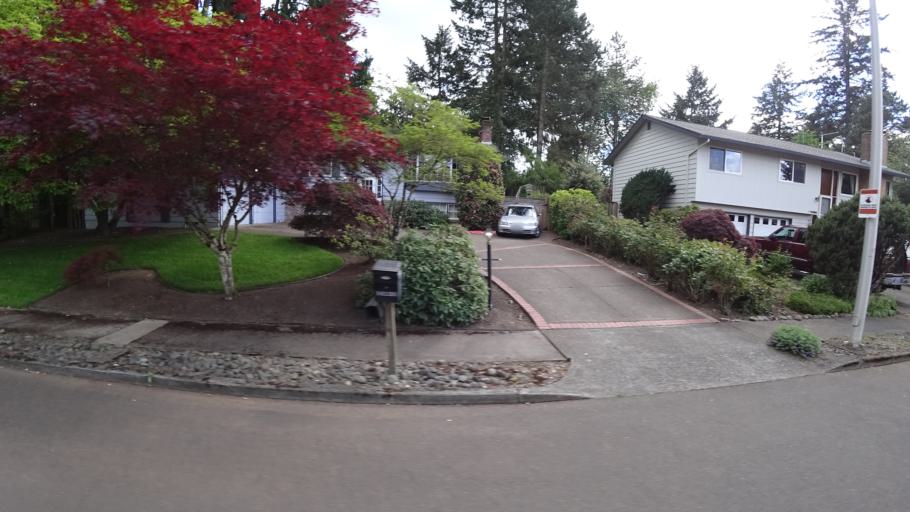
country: US
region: Oregon
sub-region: Washington County
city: Beaverton
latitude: 45.4778
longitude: -122.8223
